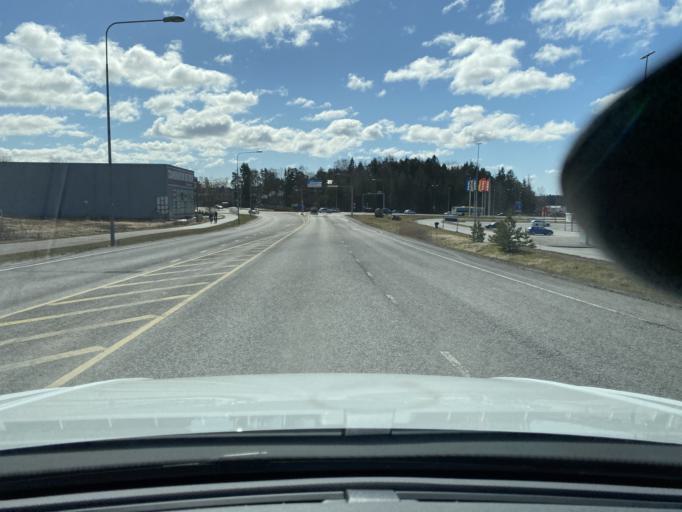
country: FI
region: Varsinais-Suomi
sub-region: Turku
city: Rusko
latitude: 60.4948
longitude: 22.2313
